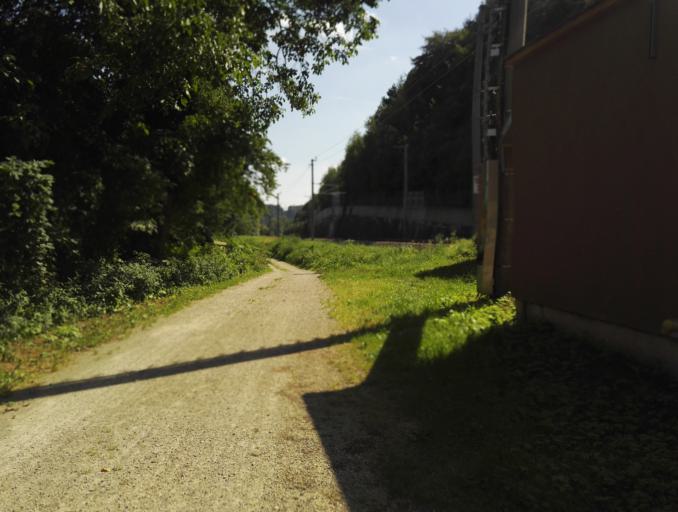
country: AT
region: Styria
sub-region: Politischer Bezirk Graz-Umgebung
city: Deutschfeistritz
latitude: 47.1532
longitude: 15.3195
